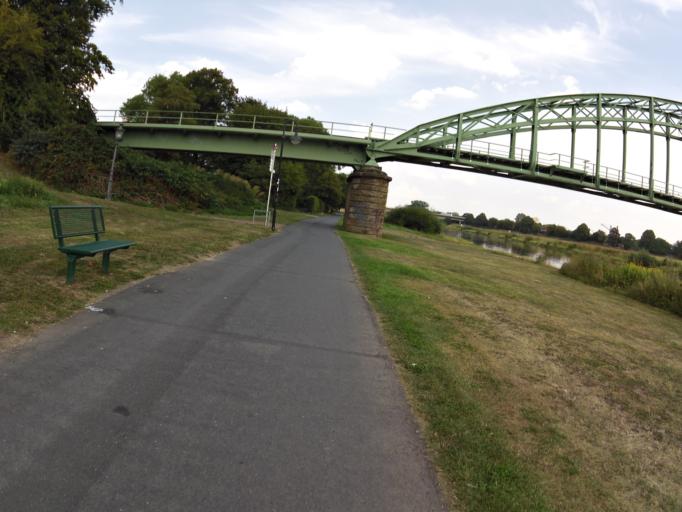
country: DE
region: North Rhine-Westphalia
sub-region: Regierungsbezirk Detmold
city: Minden
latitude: 52.2936
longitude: 8.9256
